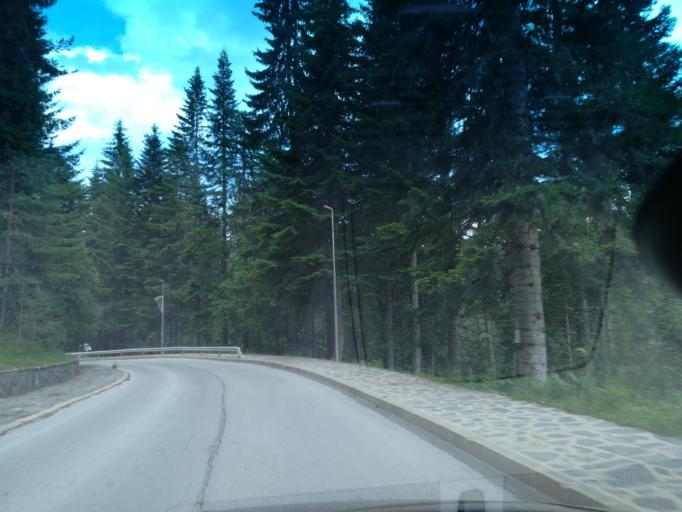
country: BG
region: Smolyan
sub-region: Obshtina Smolyan
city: Smolyan
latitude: 41.6537
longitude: 24.6922
